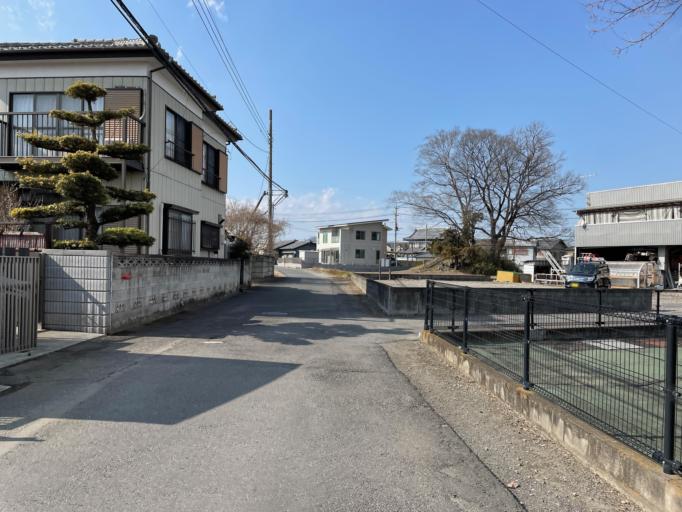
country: JP
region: Saitama
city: Yorii
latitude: 36.1242
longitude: 139.2331
